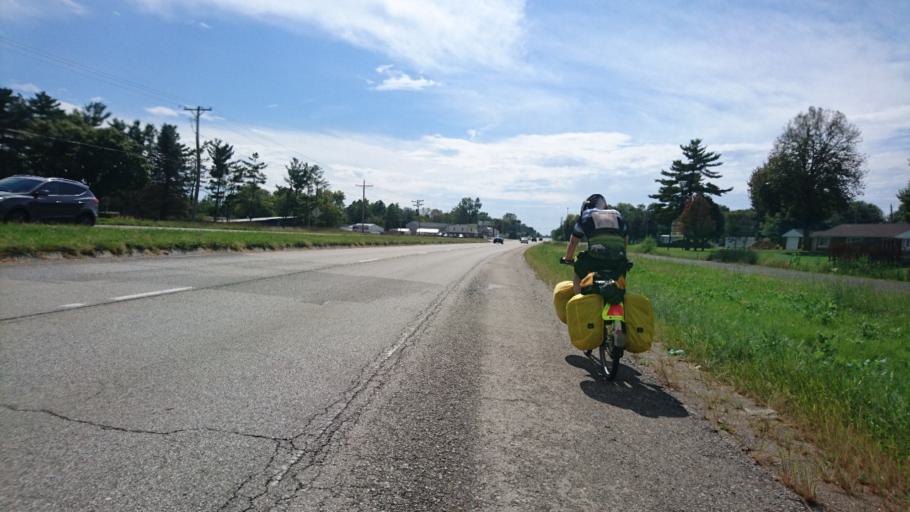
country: US
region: Illinois
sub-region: Sangamon County
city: Sherman
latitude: 39.8565
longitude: -89.6166
